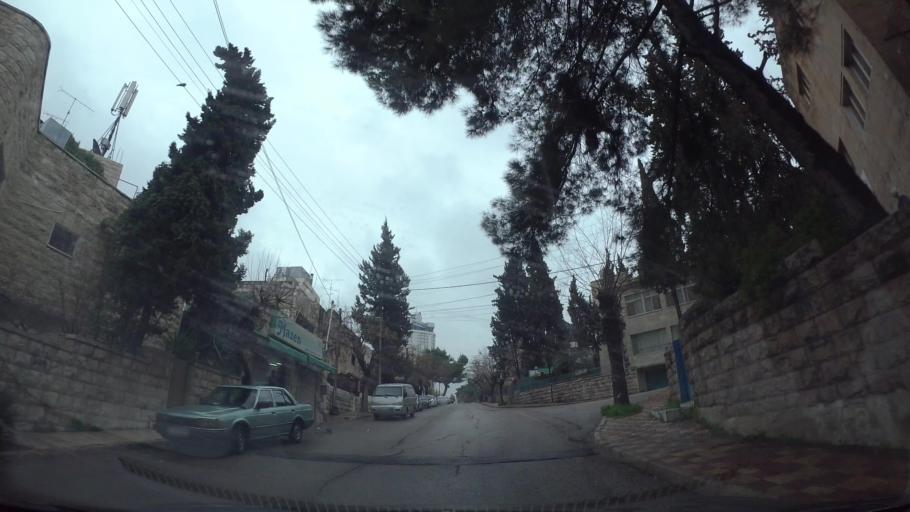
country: JO
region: Amman
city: Amman
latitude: 31.9529
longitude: 35.9155
